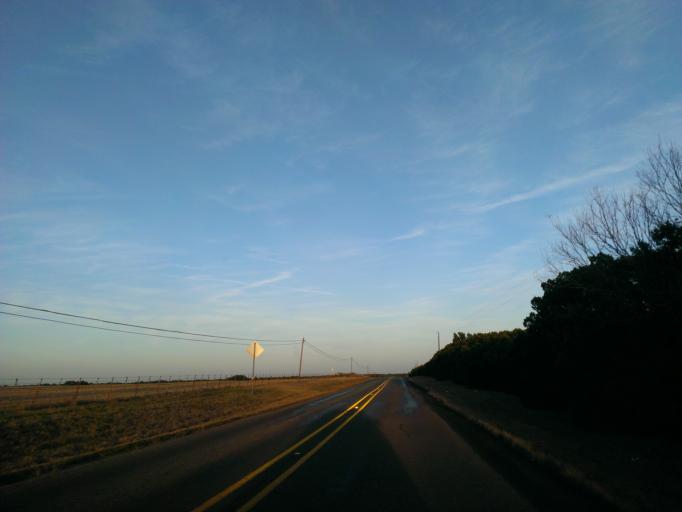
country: US
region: Texas
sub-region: Burnet County
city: Bertram
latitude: 30.7318
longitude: -98.0789
